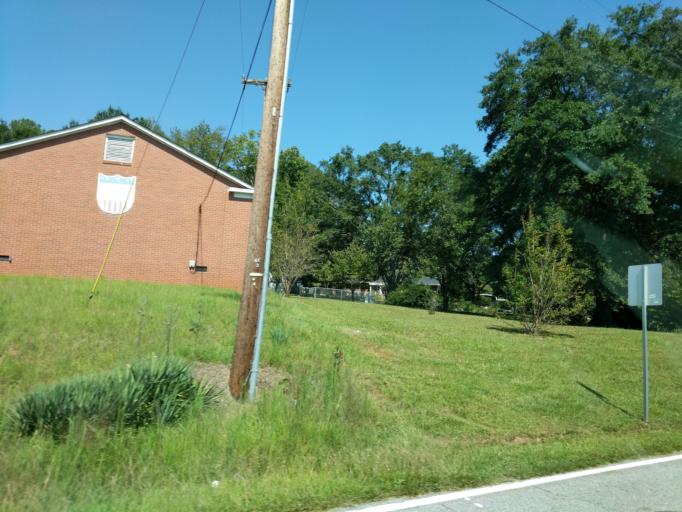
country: US
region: South Carolina
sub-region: Spartanburg County
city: Valley Falls
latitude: 35.0011
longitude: -81.9291
